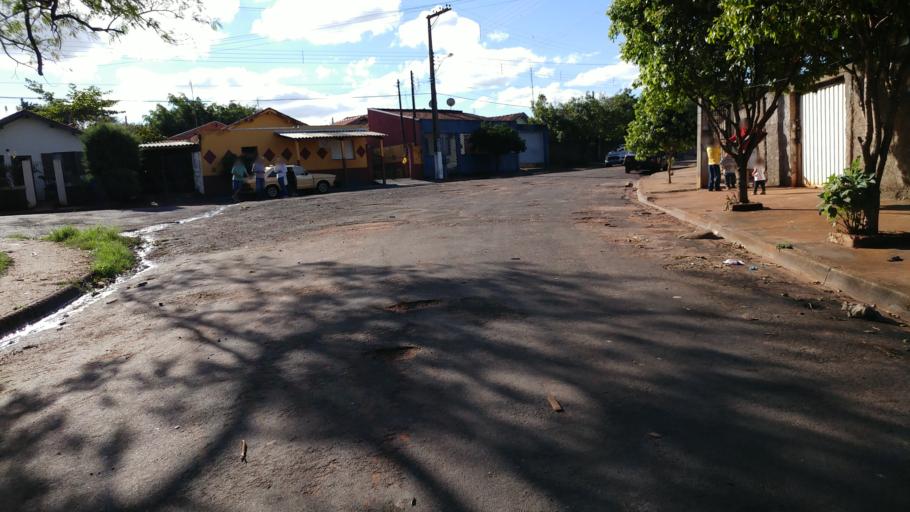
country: BR
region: Sao Paulo
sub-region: Paraguacu Paulista
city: Paraguacu Paulista
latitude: -22.4350
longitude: -50.5750
